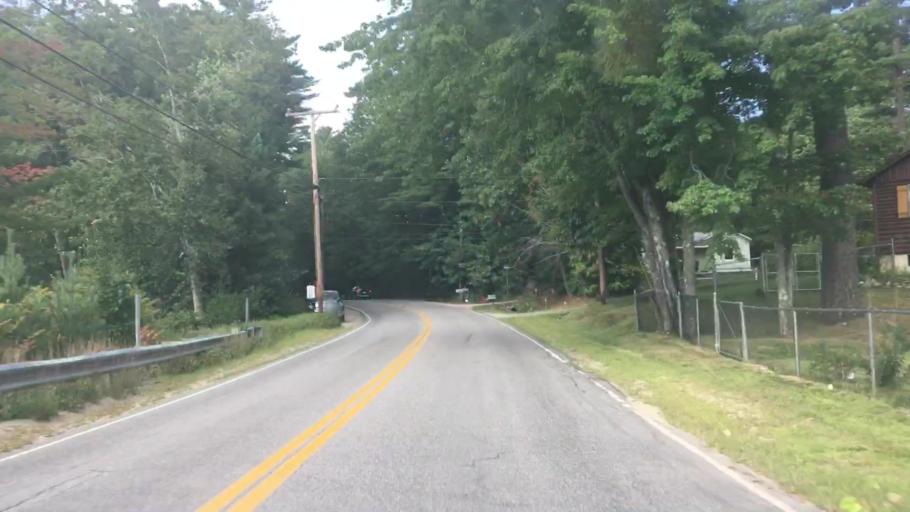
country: US
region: Maine
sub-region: Oxford County
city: Oxford
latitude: 44.1227
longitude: -70.5052
